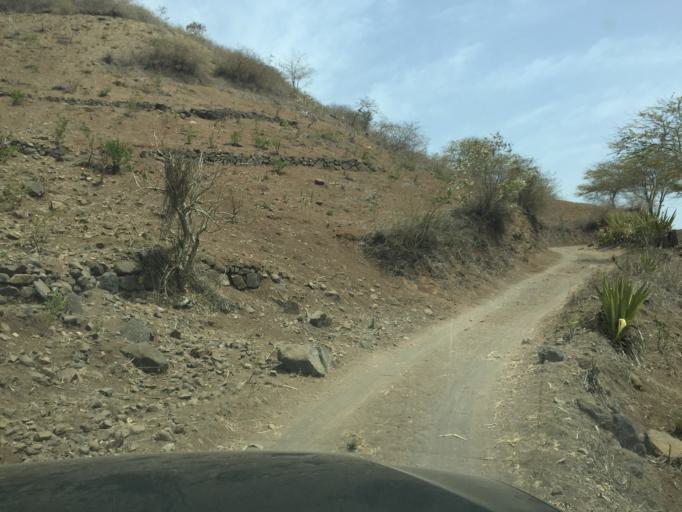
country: CV
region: Sao Salvador do Mundo
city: Picos
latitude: 15.1145
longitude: -23.6273
